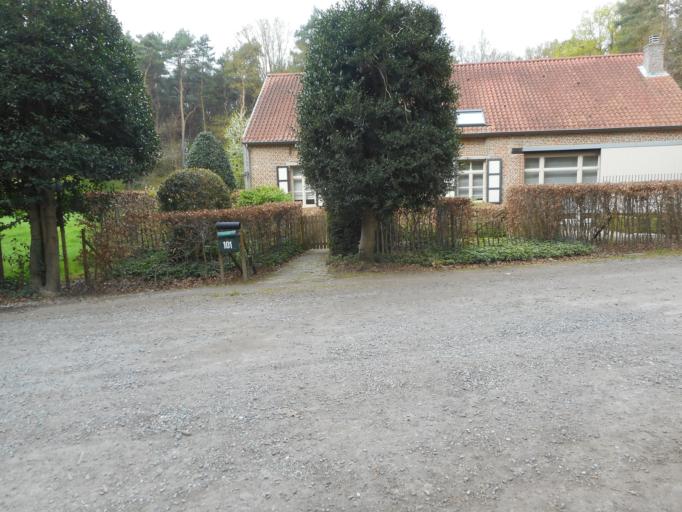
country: BE
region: Flanders
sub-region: Provincie Vlaams-Brabant
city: Aarschot
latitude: 50.9977
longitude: 4.8122
